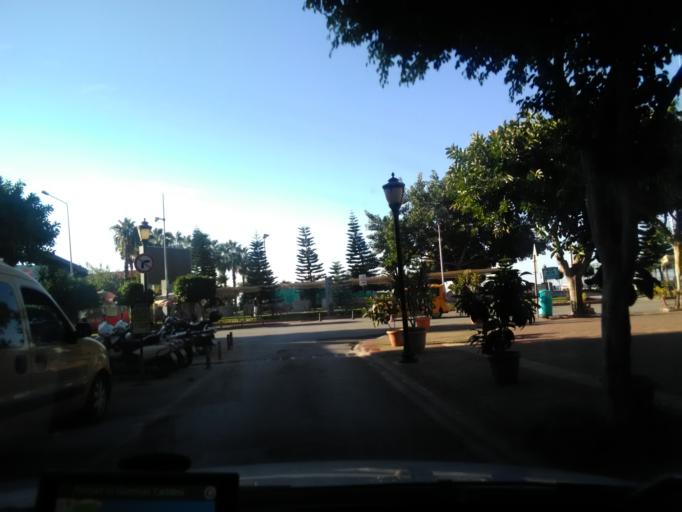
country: TR
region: Antalya
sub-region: Alanya
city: Alanya
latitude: 36.5446
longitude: 31.9873
